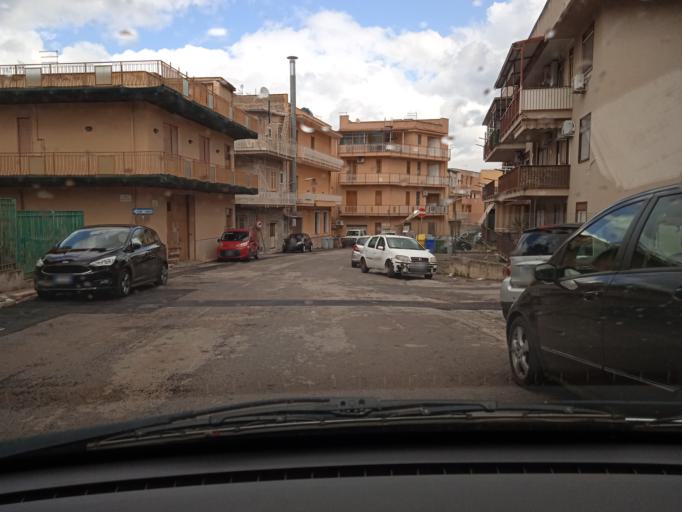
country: IT
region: Sicily
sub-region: Palermo
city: Villabate
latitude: 38.0747
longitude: 13.4406
